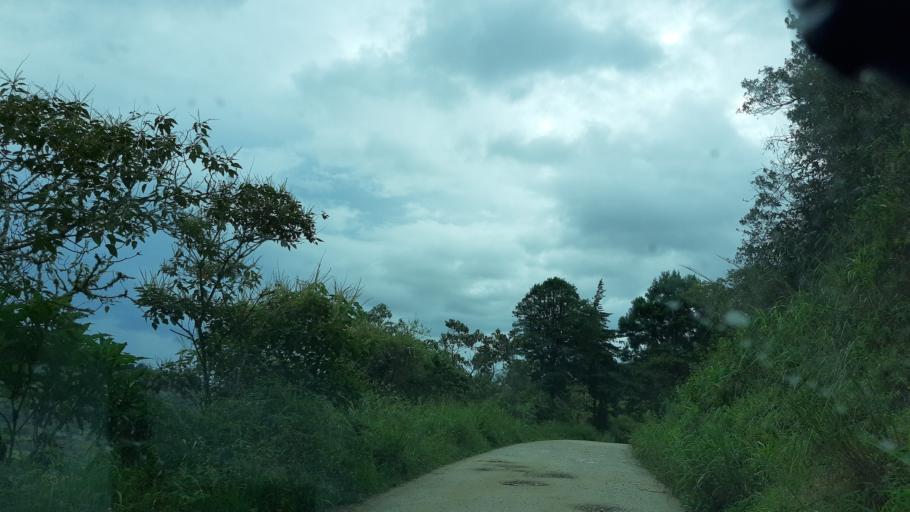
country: CO
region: Boyaca
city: Garagoa
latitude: 5.0742
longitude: -73.3606
